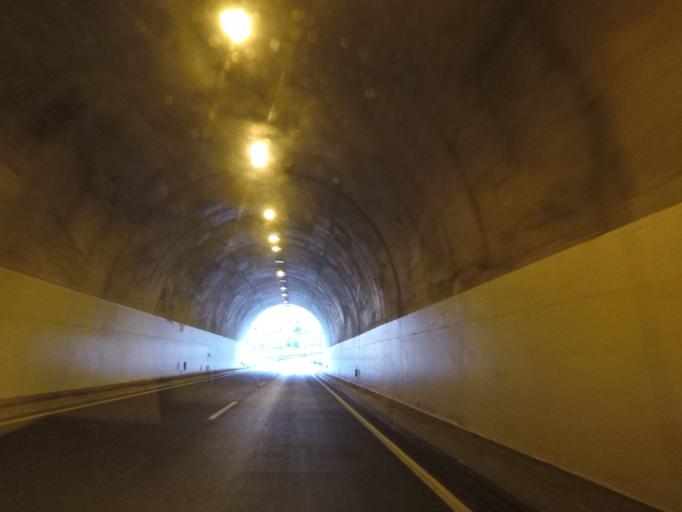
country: PT
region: Madeira
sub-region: Machico
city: Machico
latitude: 32.7306
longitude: -16.7793
